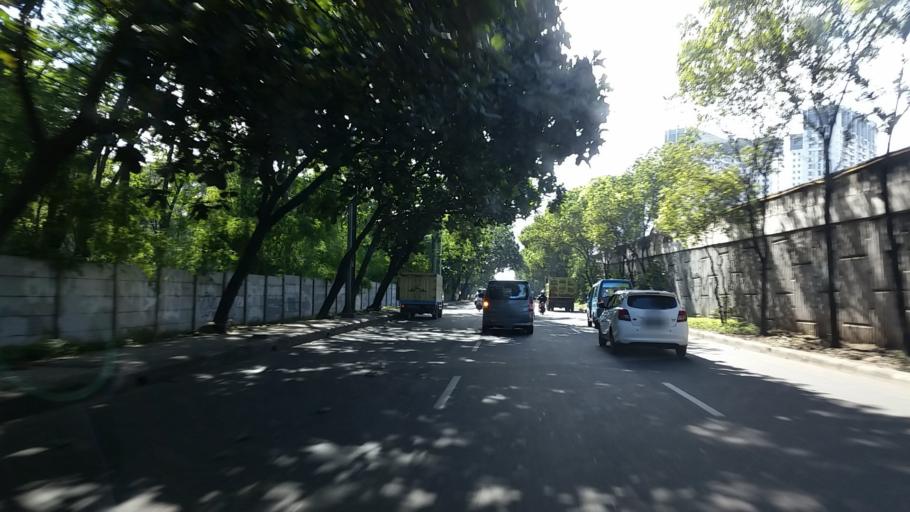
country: ID
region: Banten
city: South Tangerang
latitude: -6.2863
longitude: 106.7765
